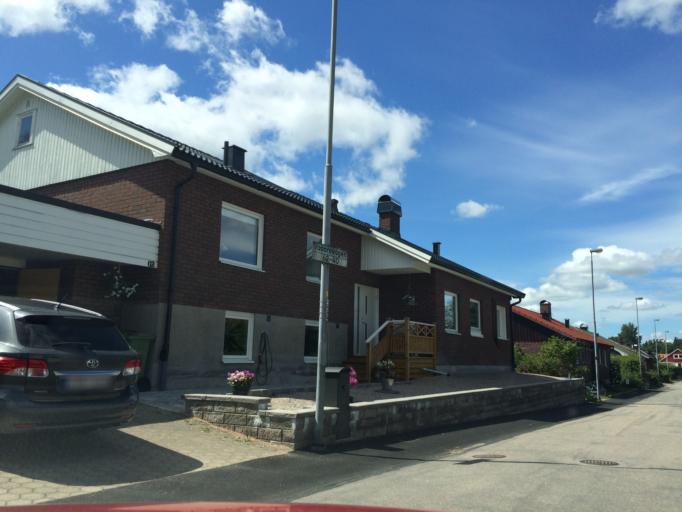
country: SE
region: Vaestra Goetaland
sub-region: Trollhattan
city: Trollhattan
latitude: 58.2784
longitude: 12.3219
